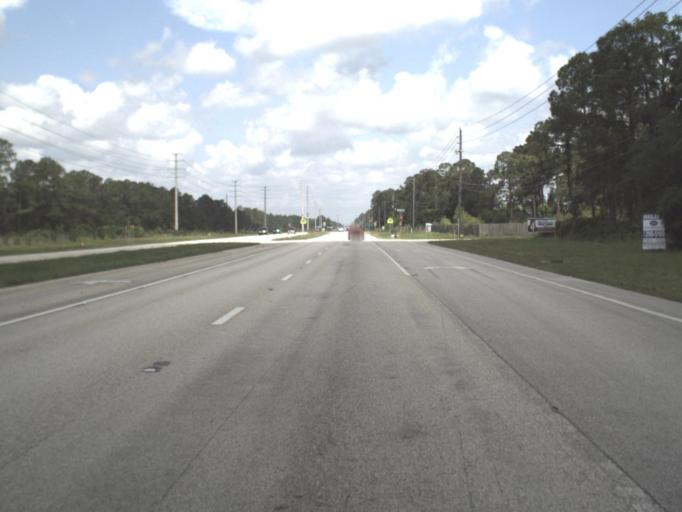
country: US
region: Florida
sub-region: Saint Johns County
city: Palm Valley
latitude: 30.0710
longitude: -81.4447
